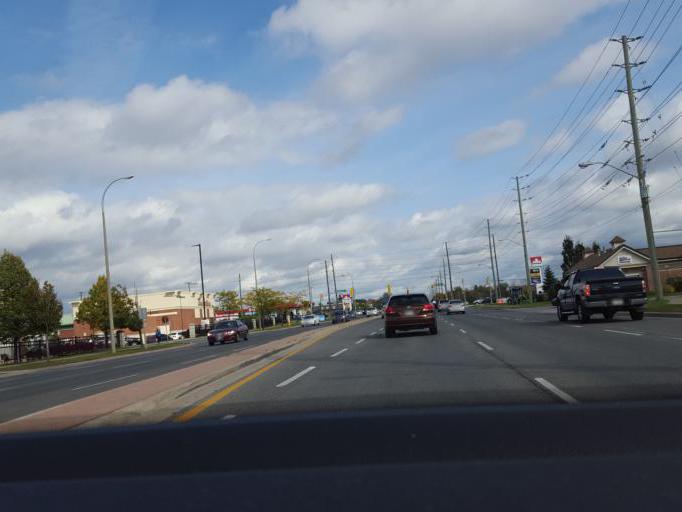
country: CA
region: Ontario
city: Ajax
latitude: 43.9148
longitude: -78.9595
